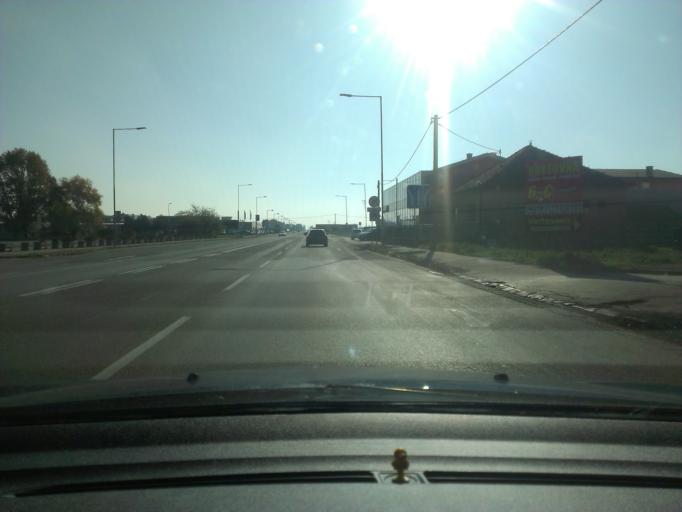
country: SK
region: Nitriansky
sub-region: Okres Nove Zamky
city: Nove Zamky
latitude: 47.9775
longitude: 18.1785
